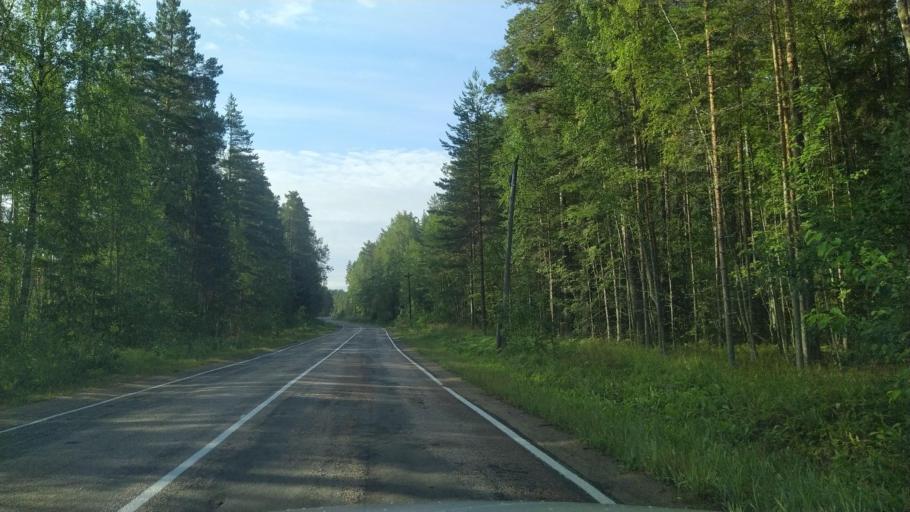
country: RU
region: Leningrad
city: Priozersk
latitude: 60.9847
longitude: 30.2661
